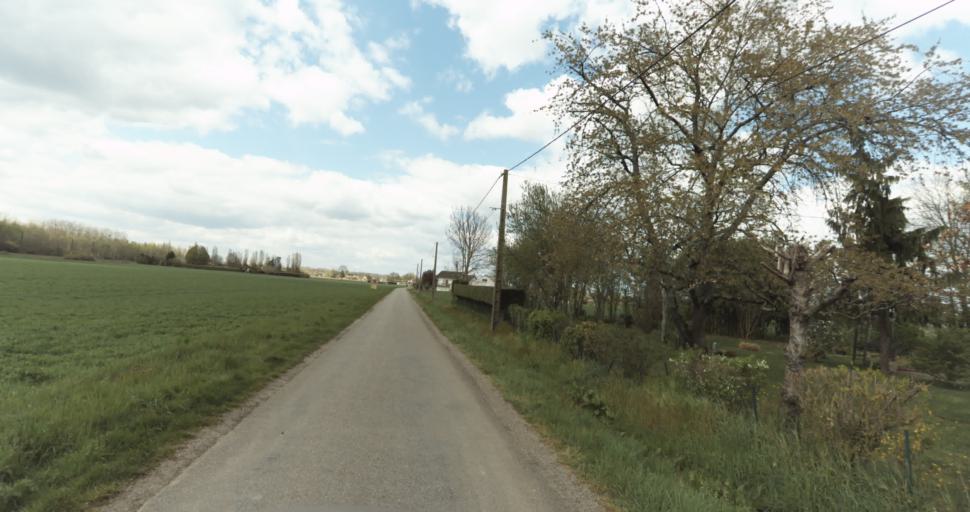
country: FR
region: Bourgogne
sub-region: Departement de la Cote-d'Or
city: Auxonne
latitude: 47.1757
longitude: 5.3946
